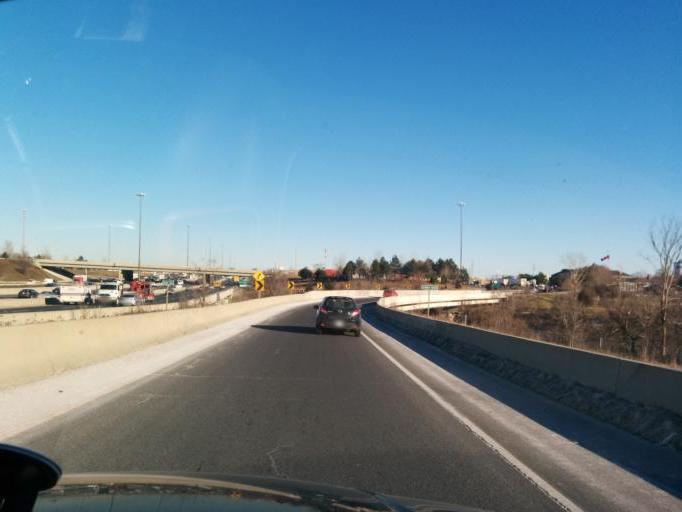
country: CA
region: Ontario
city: Etobicoke
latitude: 43.7120
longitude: -79.5398
